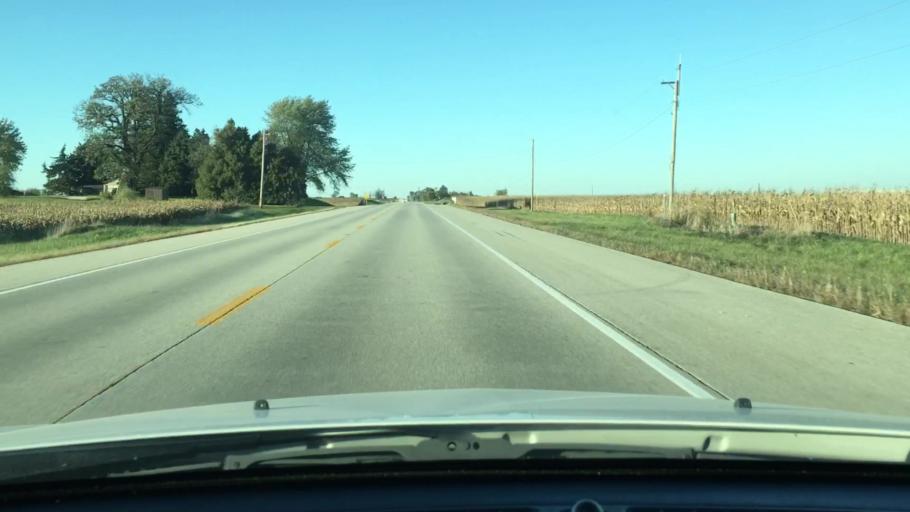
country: US
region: Illinois
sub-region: DeKalb County
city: Waterman
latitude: 41.8090
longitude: -88.7539
